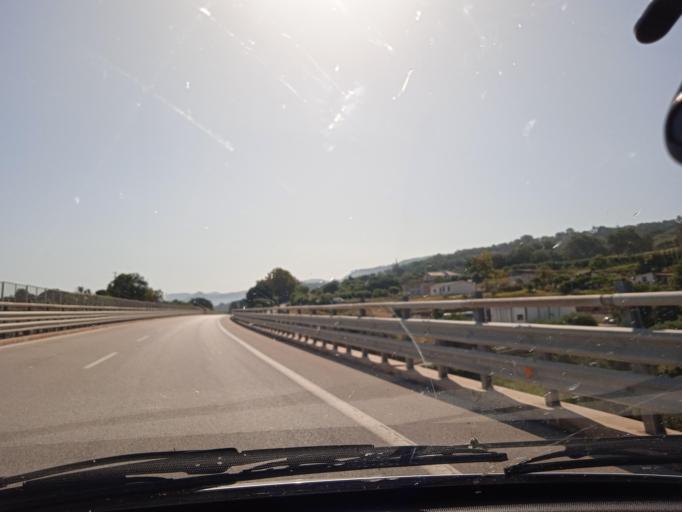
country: IT
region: Sicily
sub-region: Messina
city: Acquedolci
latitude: 38.0526
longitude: 14.5932
